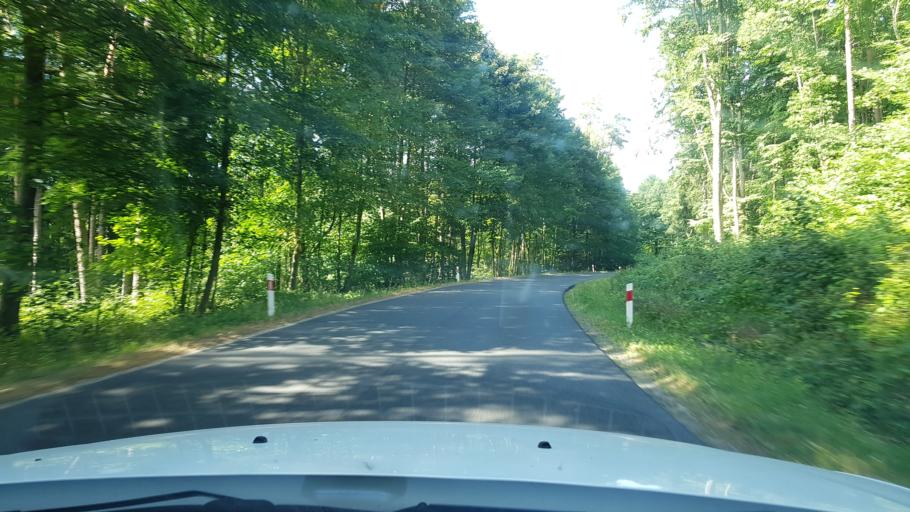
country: PL
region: West Pomeranian Voivodeship
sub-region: Powiat drawski
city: Zlocieniec
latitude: 53.5632
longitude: 16.0098
